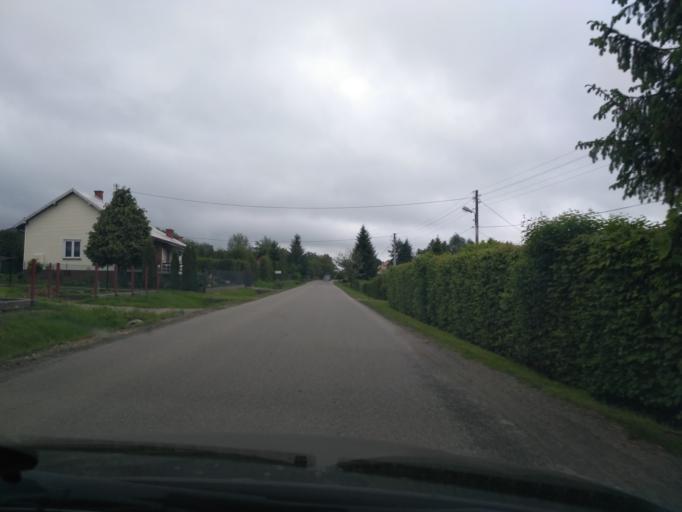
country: PL
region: Subcarpathian Voivodeship
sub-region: Powiat jasielski
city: Tarnowiec
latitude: 49.8023
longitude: 21.5343
